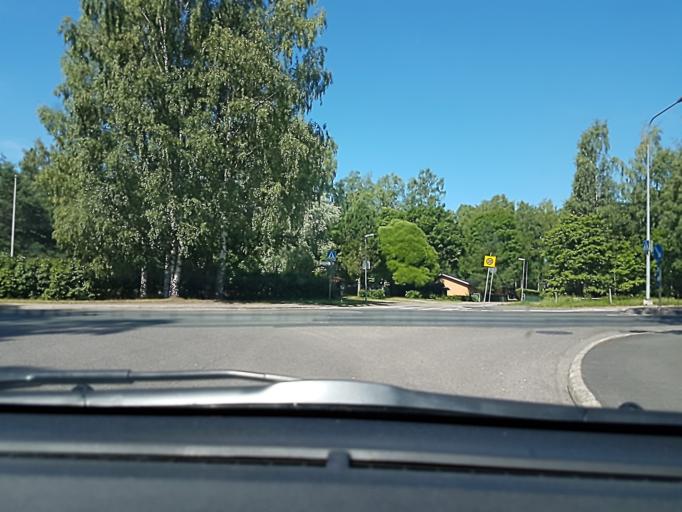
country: FI
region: Uusimaa
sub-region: Helsinki
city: Vantaa
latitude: 60.3132
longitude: 25.0329
